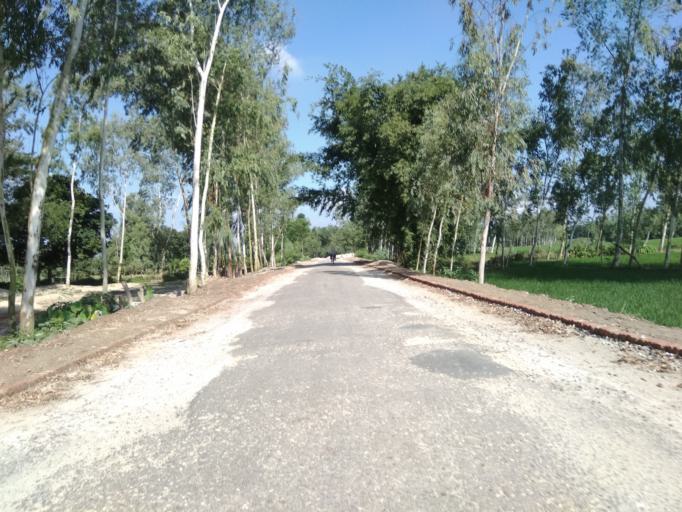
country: BD
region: Rangpur Division
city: Panchagarh
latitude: 26.2552
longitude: 88.6212
